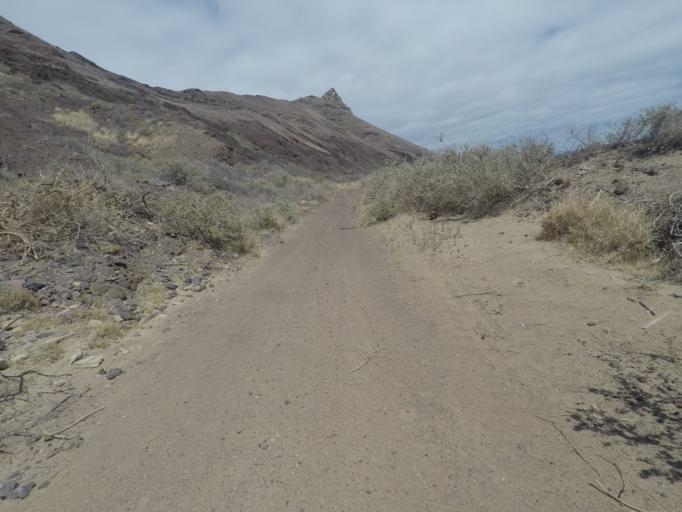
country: PT
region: Madeira
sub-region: Porto Santo
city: Vila de Porto Santo
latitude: 33.0629
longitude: -16.3059
